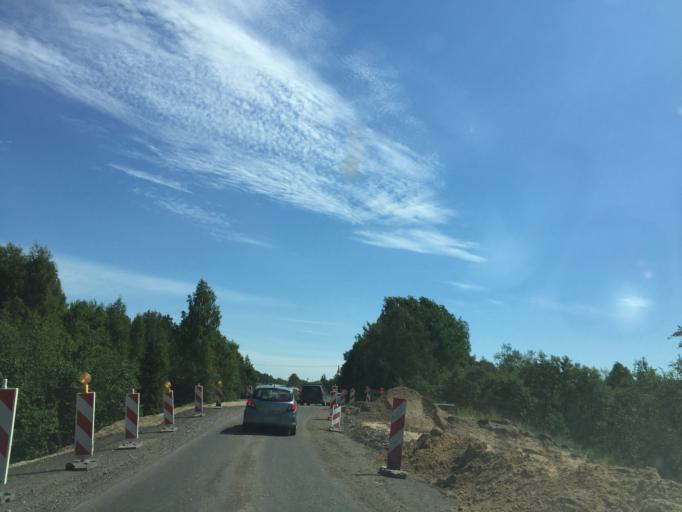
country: LV
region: Saldus Rajons
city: Saldus
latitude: 56.6712
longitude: 22.3597
